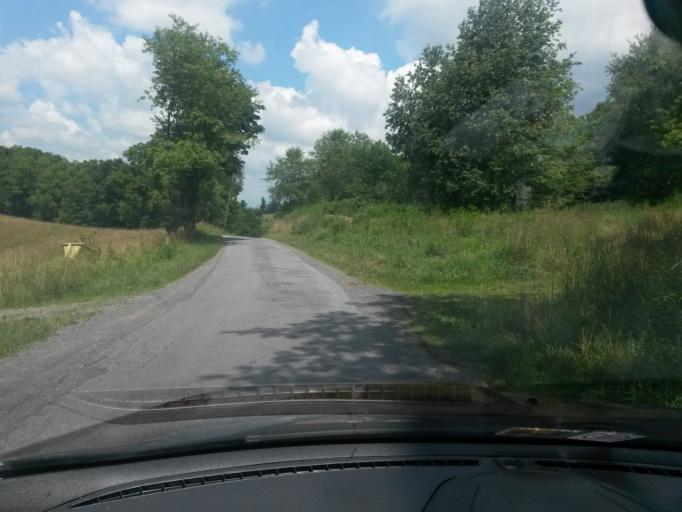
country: US
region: West Virginia
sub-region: Monroe County
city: Union
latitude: 37.5662
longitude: -80.4918
